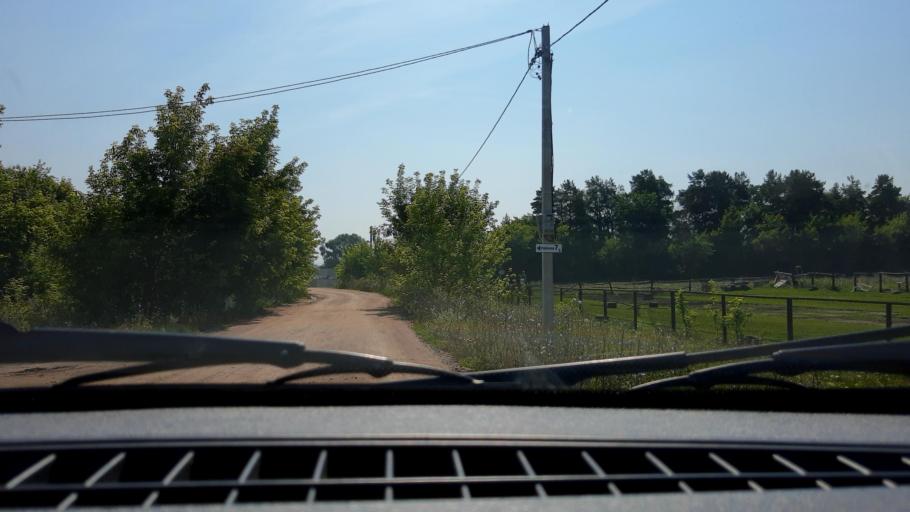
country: RU
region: Bashkortostan
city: Mikhaylovka
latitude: 54.7849
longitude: 55.8437
